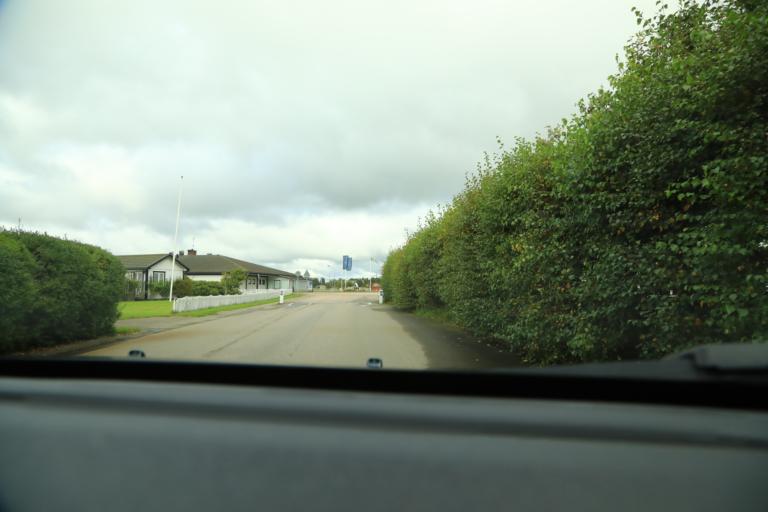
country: SE
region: Halland
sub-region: Varbergs Kommun
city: Tvaaker
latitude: 57.0112
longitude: 12.3547
